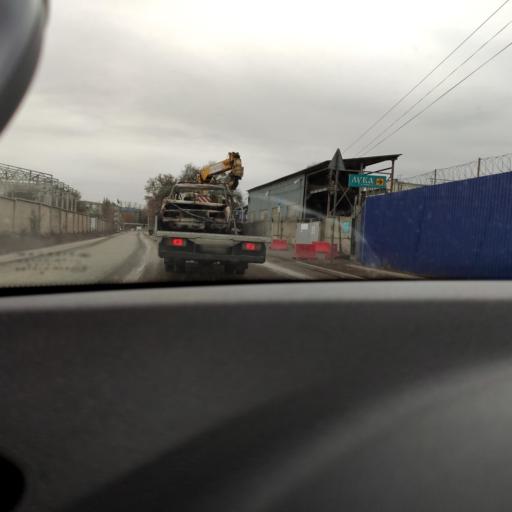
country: RU
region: Samara
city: Smyshlyayevka
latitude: 53.2075
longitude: 50.3024
